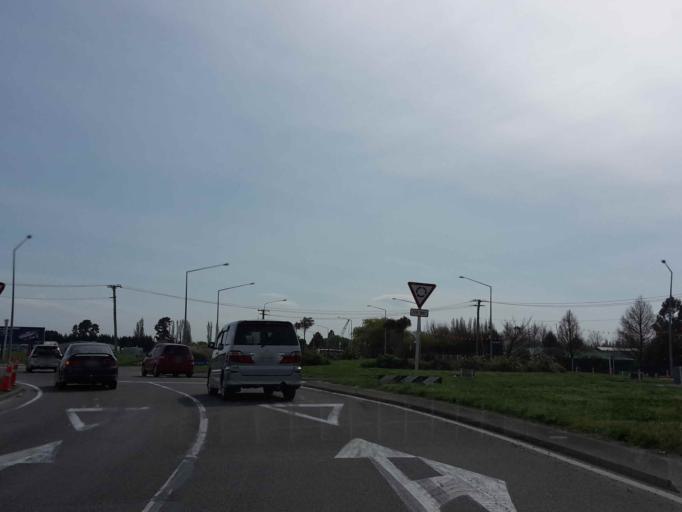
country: NZ
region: Canterbury
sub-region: Christchurch City
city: Christchurch
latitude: -43.4867
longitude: 172.5533
